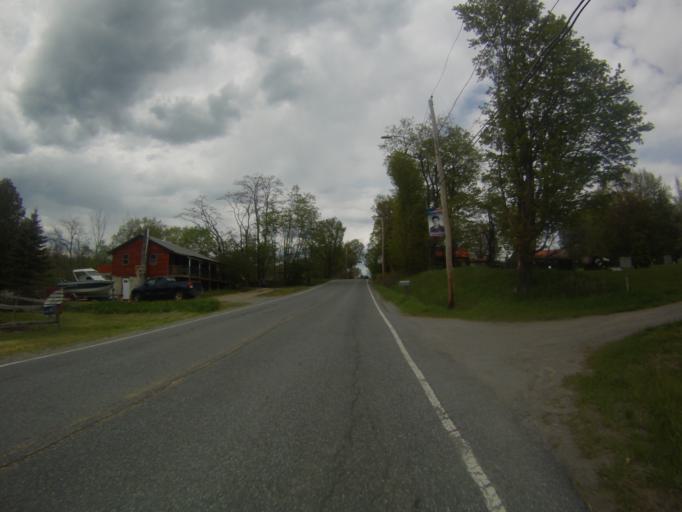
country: US
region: New York
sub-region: Essex County
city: Port Henry
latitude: 44.0398
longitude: -73.5039
